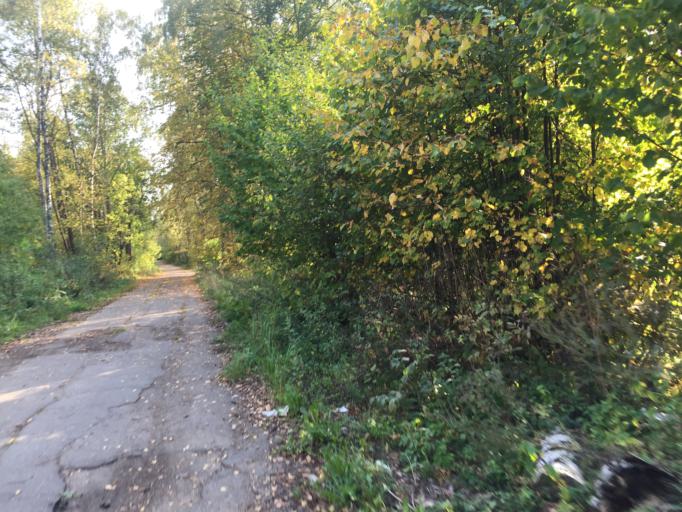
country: RU
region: Moscow
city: Babushkin
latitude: 55.8495
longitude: 37.7194
